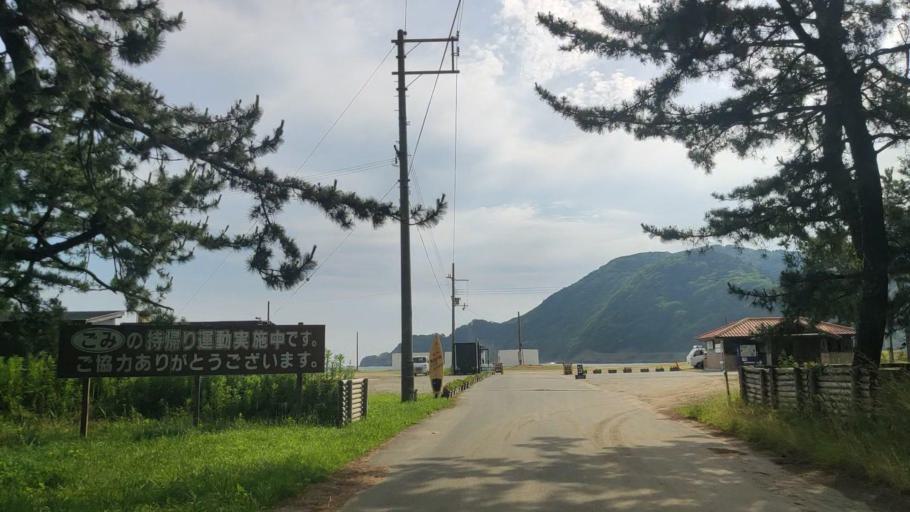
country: JP
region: Hyogo
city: Toyooka
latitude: 35.6442
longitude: 134.8355
